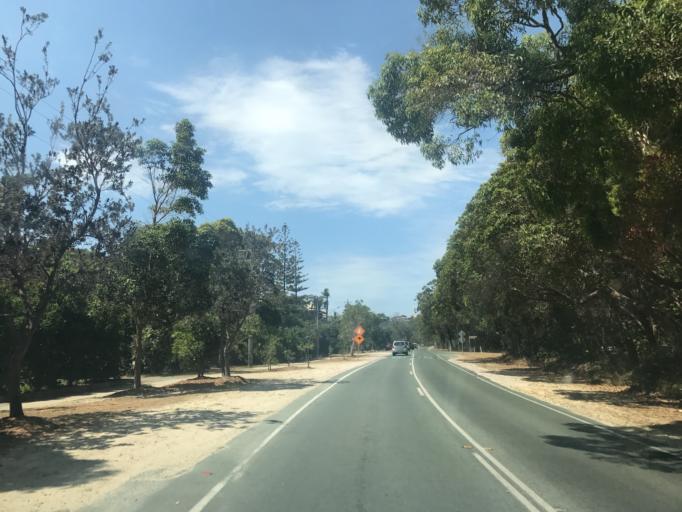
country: AU
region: Queensland
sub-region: Redland
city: Victoria Point
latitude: -27.4235
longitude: 153.5166
